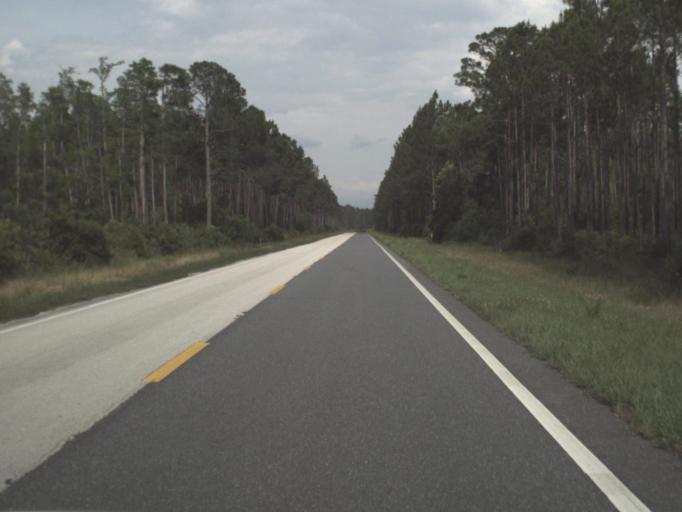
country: US
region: Florida
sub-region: Baker County
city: Macclenny
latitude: 30.5667
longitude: -82.4093
